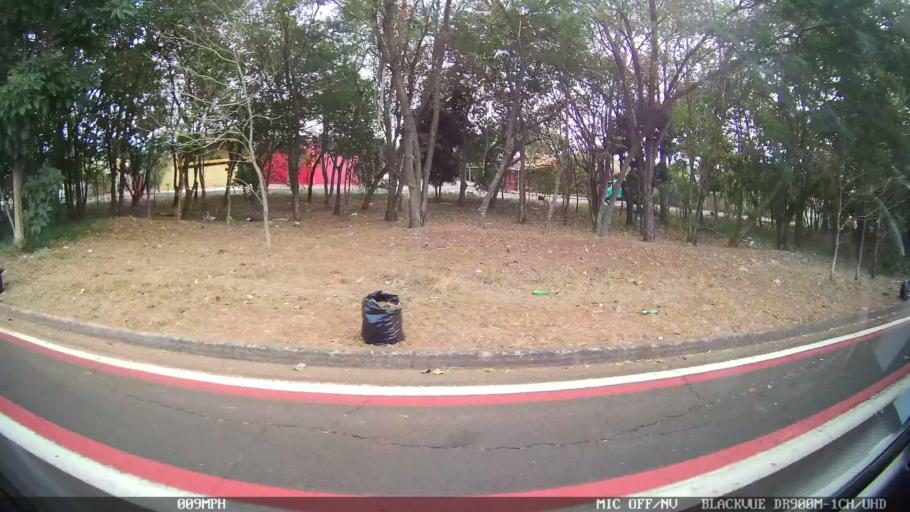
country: BR
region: Sao Paulo
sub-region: Catanduva
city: Catanduva
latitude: -21.1500
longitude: -48.9939
